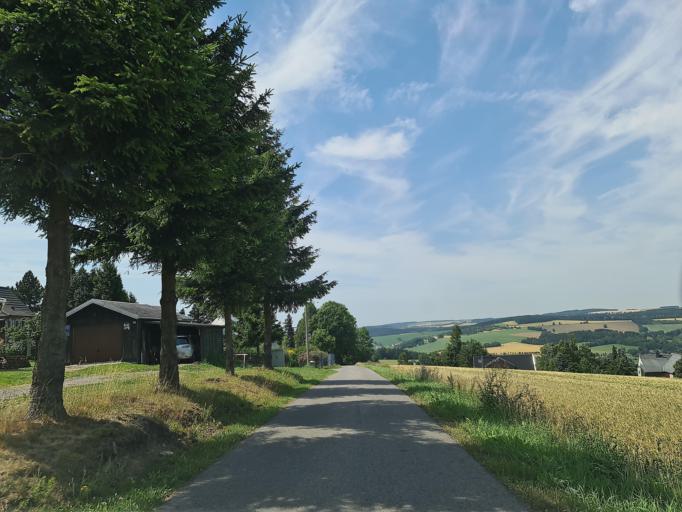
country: DE
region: Saxony
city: Neuhausen
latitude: 50.6612
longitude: 13.4704
